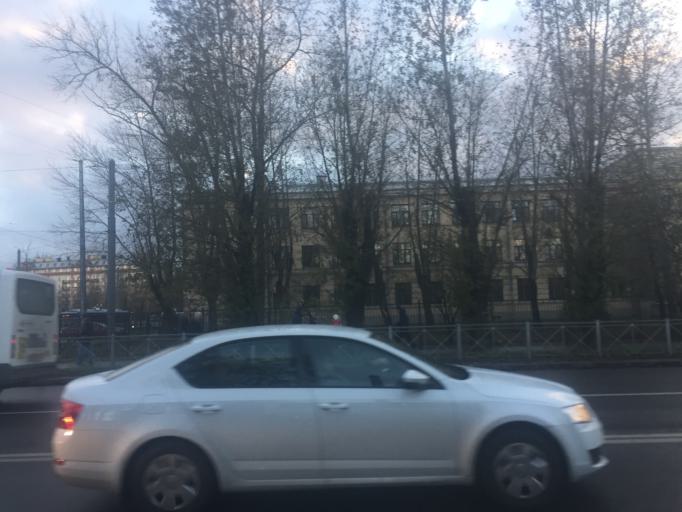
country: RU
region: St.-Petersburg
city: Obukhovo
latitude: 59.8788
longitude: 30.4407
